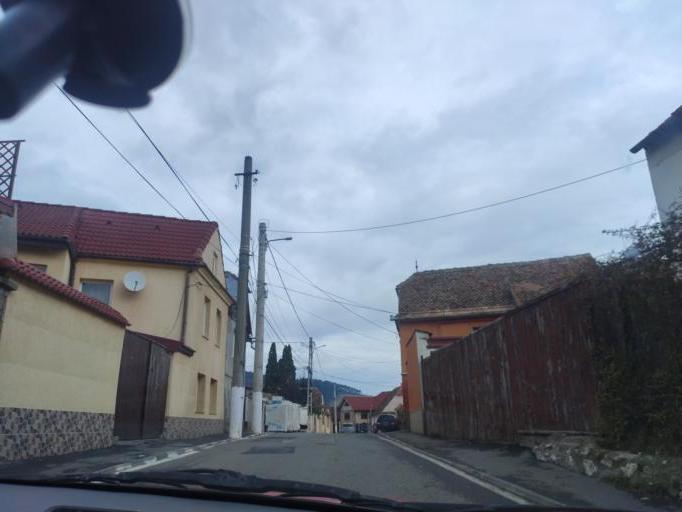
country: RO
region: Brasov
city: Codlea
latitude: 45.6965
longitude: 25.4422
